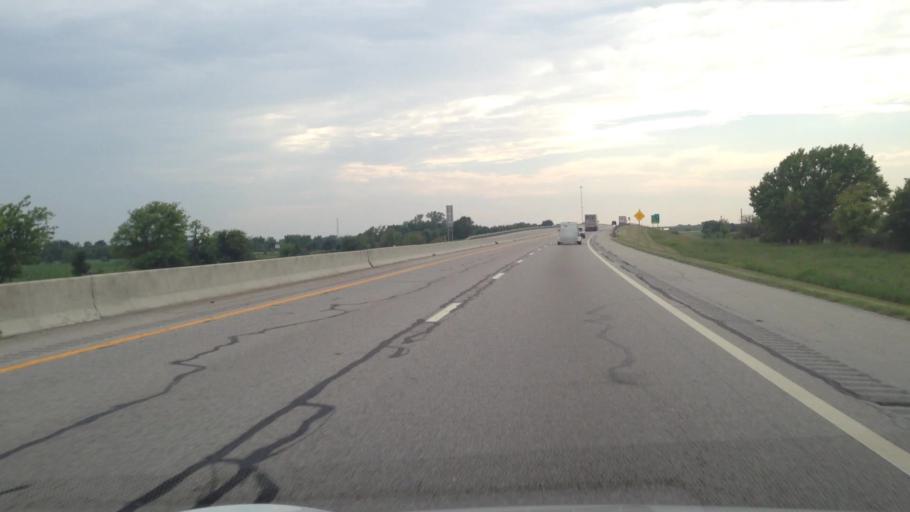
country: US
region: Oklahoma
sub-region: Ottawa County
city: Afton
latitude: 36.7271
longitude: -94.9229
